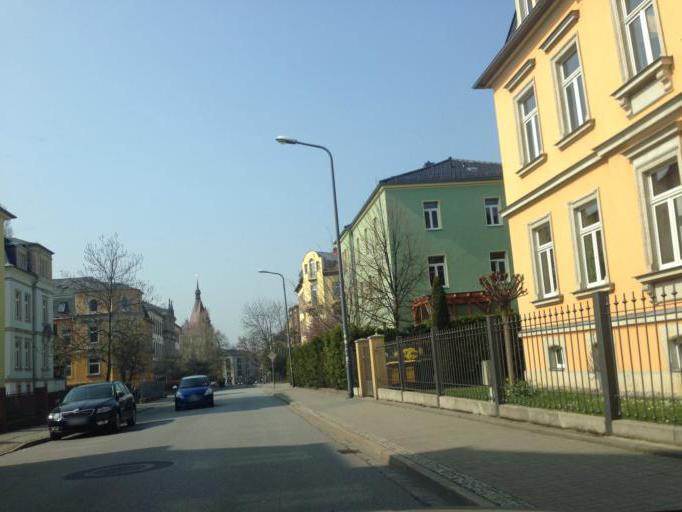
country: DE
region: Saxony
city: Dresden
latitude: 51.0284
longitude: 13.7107
